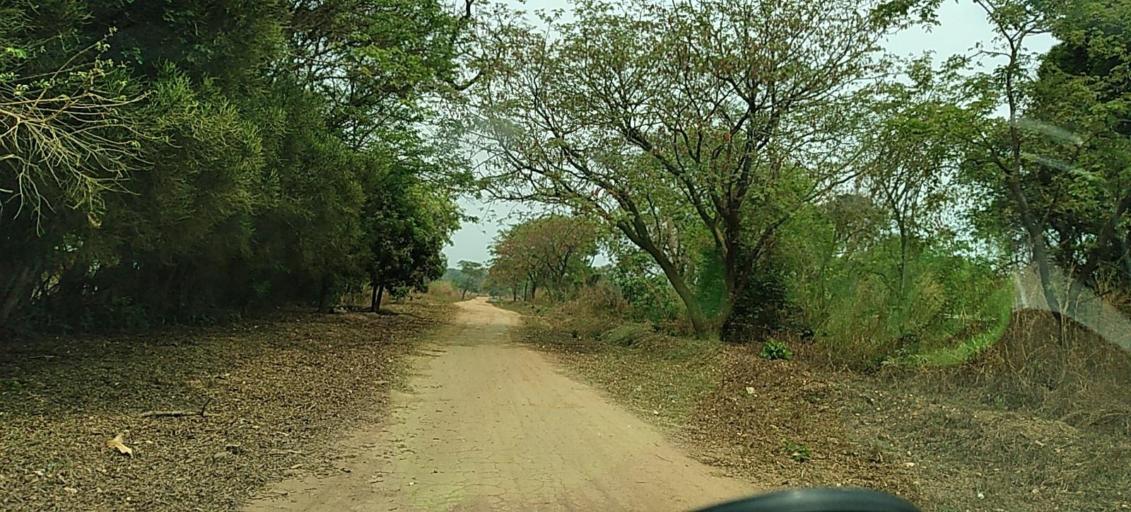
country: ZM
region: North-Western
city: Solwezi
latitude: -12.7908
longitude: 26.5298
